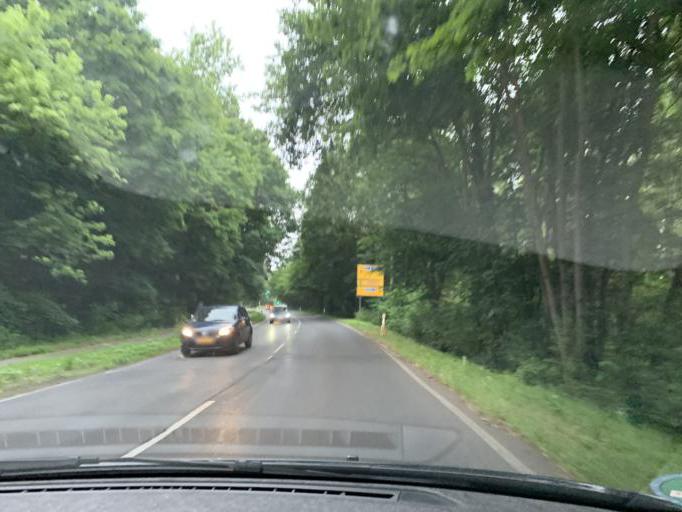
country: DE
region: North Rhine-Westphalia
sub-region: Regierungsbezirk Koln
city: Kerpen
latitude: 50.8857
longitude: 6.7181
